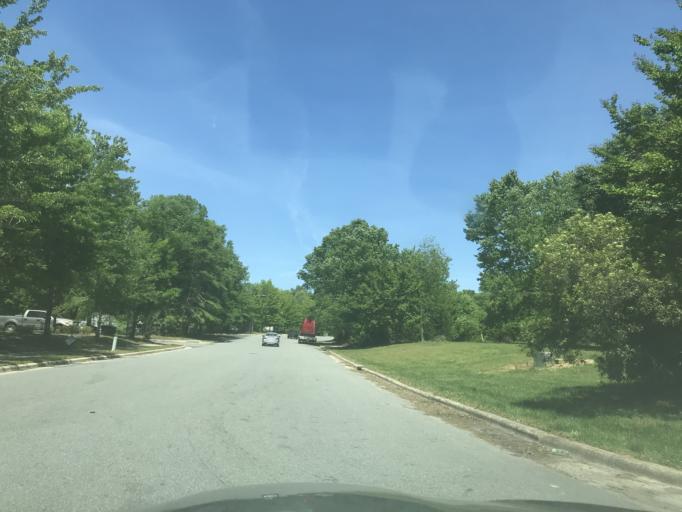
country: US
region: North Carolina
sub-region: Wake County
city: Raleigh
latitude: 35.7991
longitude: -78.5821
